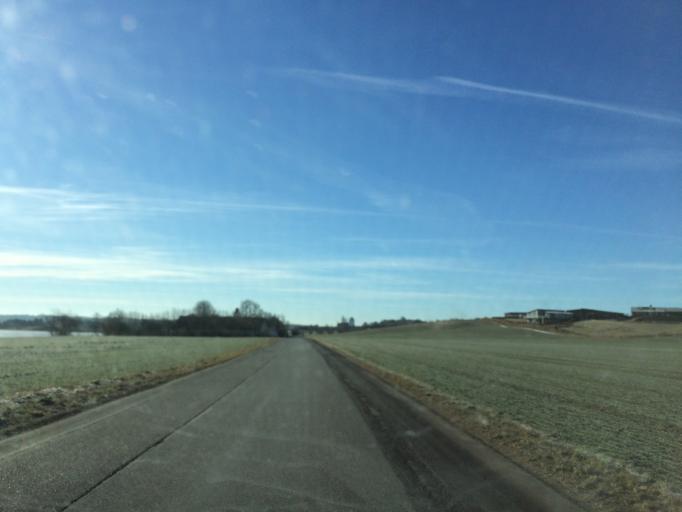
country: DK
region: North Denmark
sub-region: Mariagerfjord Kommune
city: Hobro
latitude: 56.5987
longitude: 9.6306
